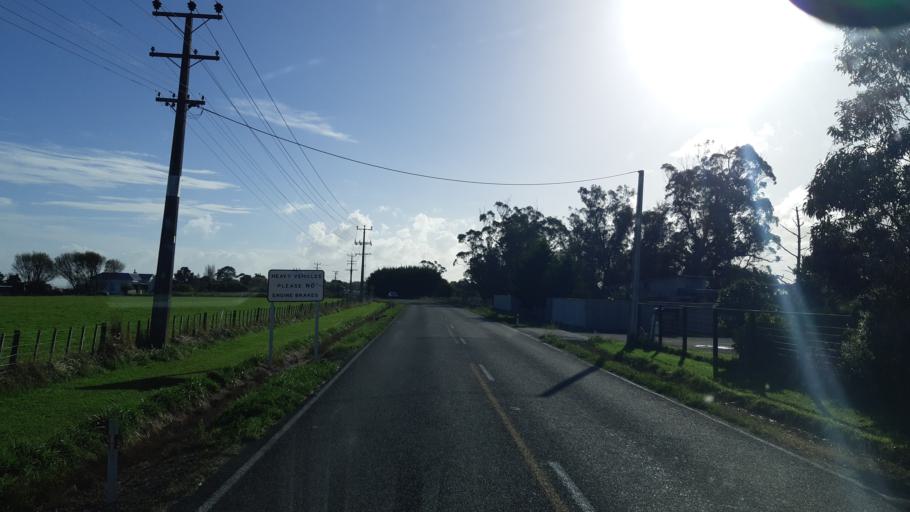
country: NZ
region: Manawatu-Wanganui
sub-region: Wanganui District
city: Wanganui
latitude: -39.9407
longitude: 175.0821
